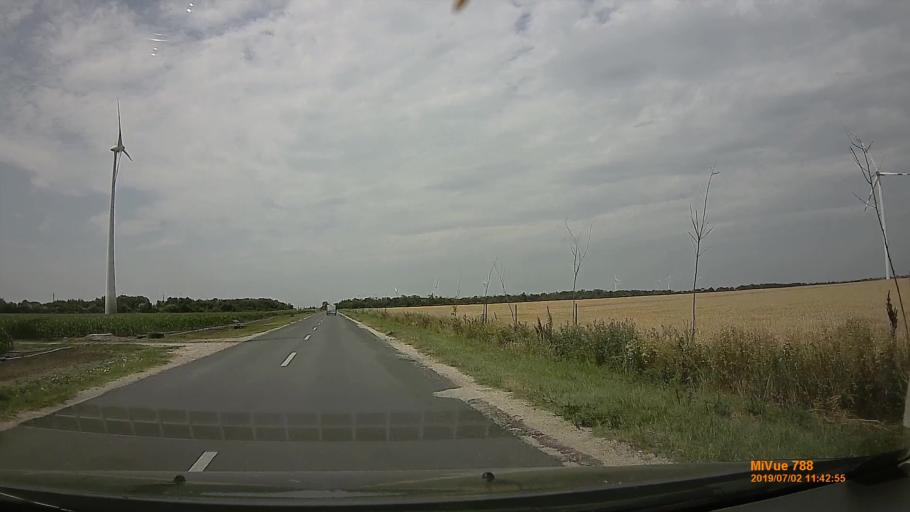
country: HU
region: Gyor-Moson-Sopron
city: Mosonmagyarovar
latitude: 47.8783
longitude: 17.2258
